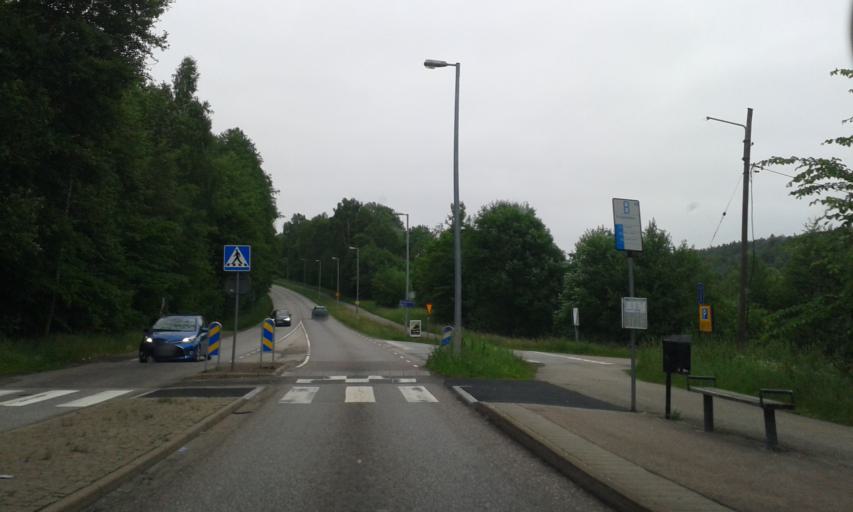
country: SE
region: Vaestra Goetaland
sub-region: Goteborg
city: Eriksbo
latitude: 57.7591
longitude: 12.0749
